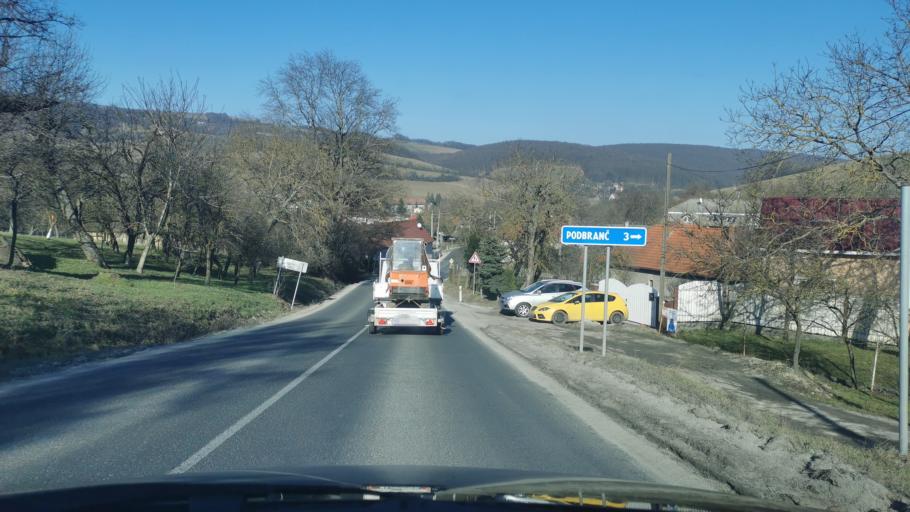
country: SK
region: Trnavsky
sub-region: Okres Senica
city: Senica
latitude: 48.7382
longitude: 17.4352
